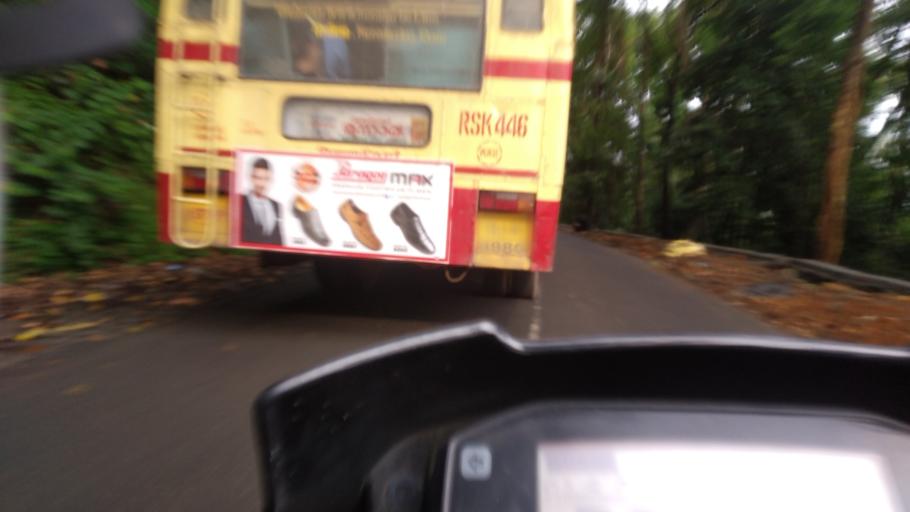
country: IN
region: Kerala
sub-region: Idukki
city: Kuttampuzha
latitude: 10.0660
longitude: 76.7724
